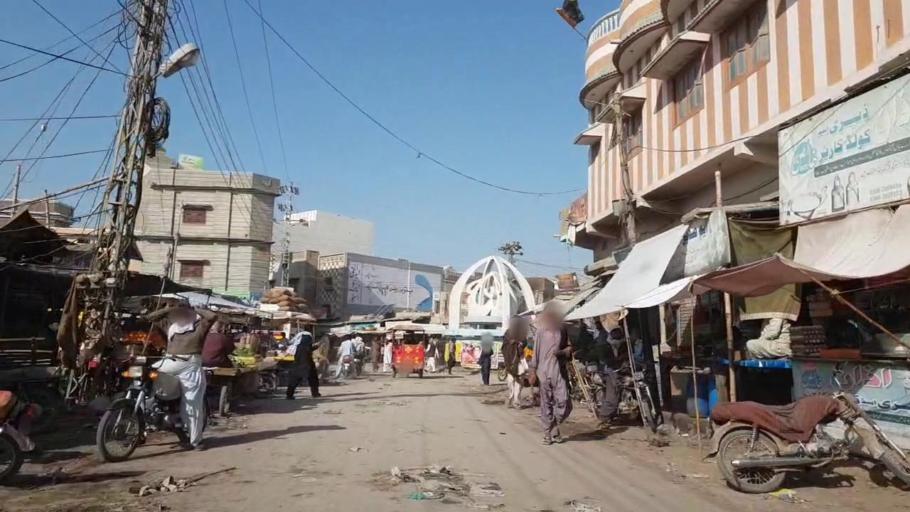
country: PK
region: Sindh
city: Digri
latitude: 25.1551
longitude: 69.1117
